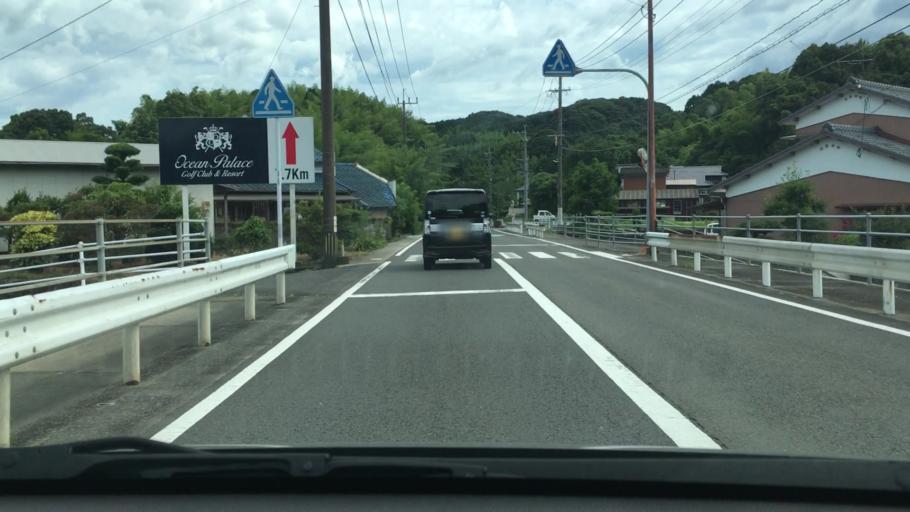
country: JP
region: Nagasaki
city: Togitsu
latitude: 32.9338
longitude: 129.7834
